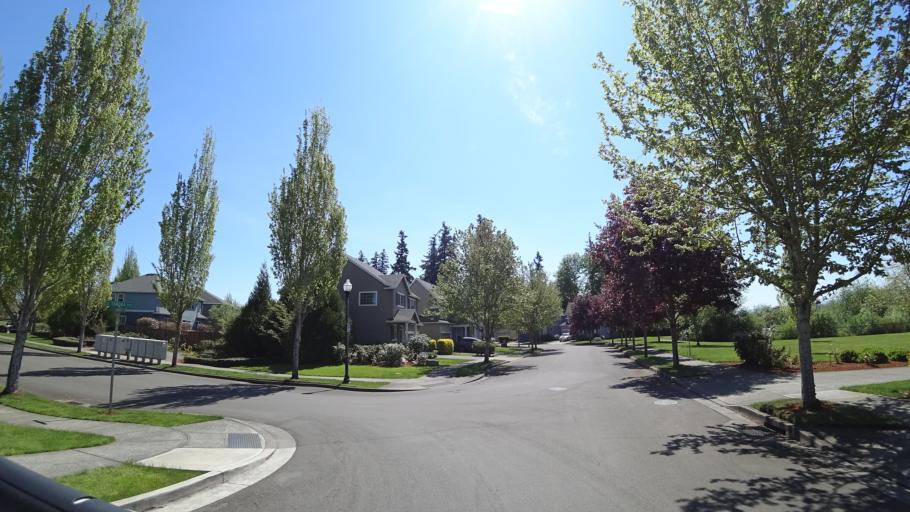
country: US
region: Oregon
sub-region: Washington County
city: Hillsboro
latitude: 45.5081
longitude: -122.9764
